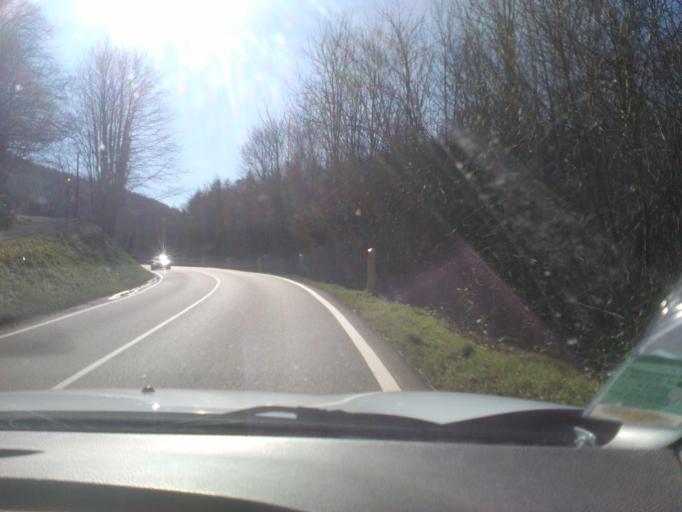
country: FR
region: Alsace
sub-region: Departement du Bas-Rhin
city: Rothau
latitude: 48.4507
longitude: 7.1980
